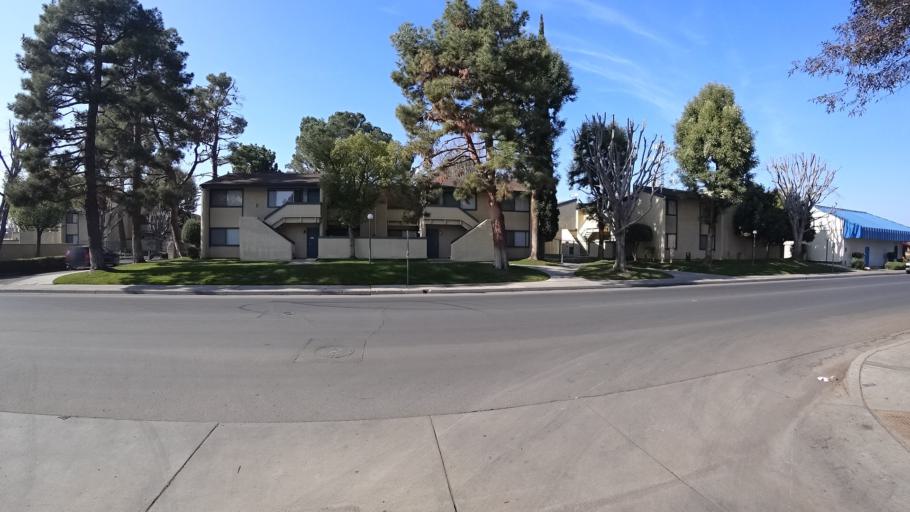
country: US
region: California
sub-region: Kern County
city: Bakersfield
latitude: 35.3310
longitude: -119.0433
